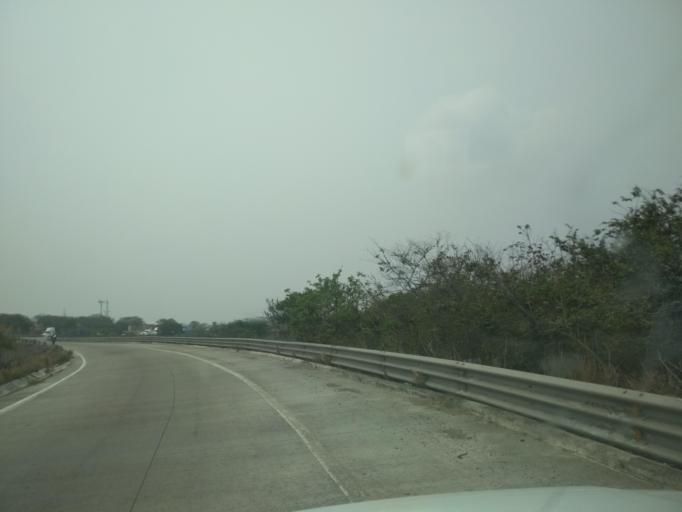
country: MX
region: Veracruz
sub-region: Veracruz
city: Fraccionamiento Geovillas los Pinos
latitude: 19.2180
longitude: -96.2218
